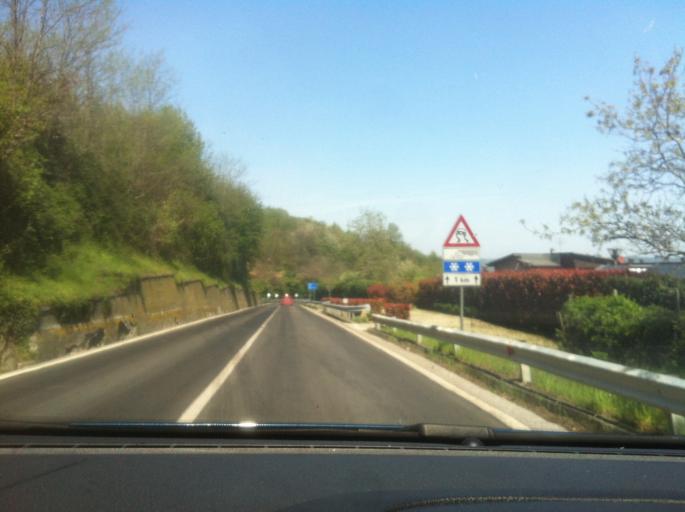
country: IT
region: Piedmont
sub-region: Provincia di Torino
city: Candia Canavese
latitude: 45.3323
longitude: 7.8871
